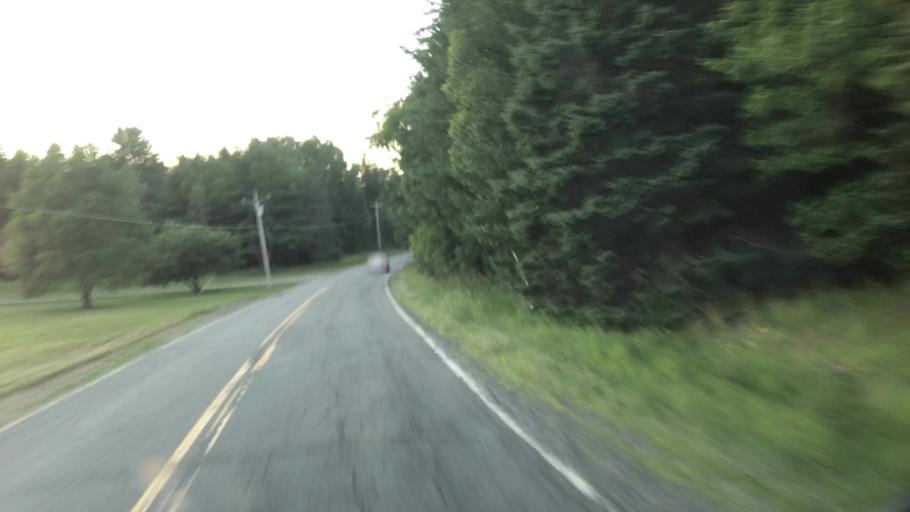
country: US
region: Maine
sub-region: Penobscot County
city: Medway
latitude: 45.6066
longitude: -68.2557
